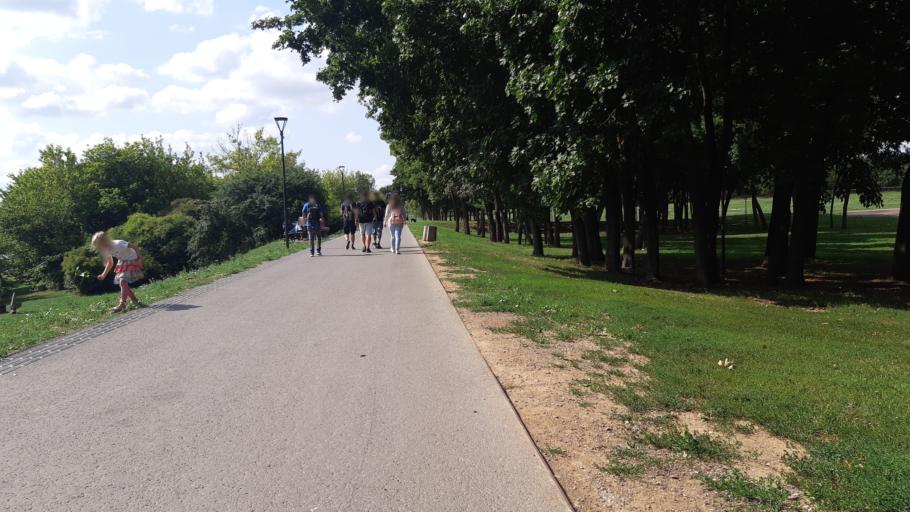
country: LT
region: Kauno apskritis
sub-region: Kaunas
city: Kaunas
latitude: 54.8962
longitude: 23.8811
